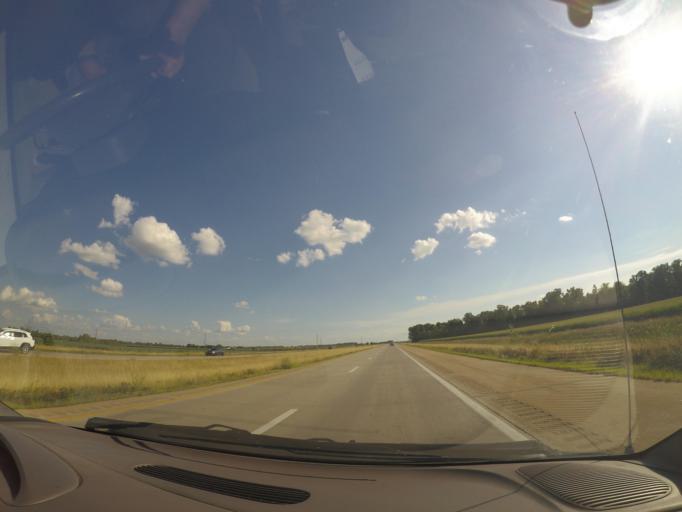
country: US
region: Ohio
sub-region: Lucas County
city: Whitehouse
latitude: 41.4849
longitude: -83.7732
